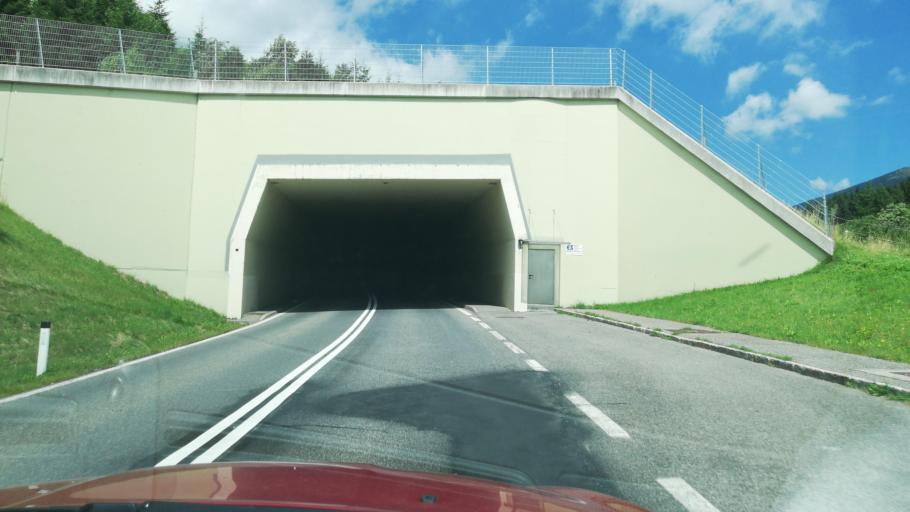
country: AT
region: Styria
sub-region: Politischer Bezirk Murtal
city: Sankt Johann am Tauern
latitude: 47.3725
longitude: 14.4613
